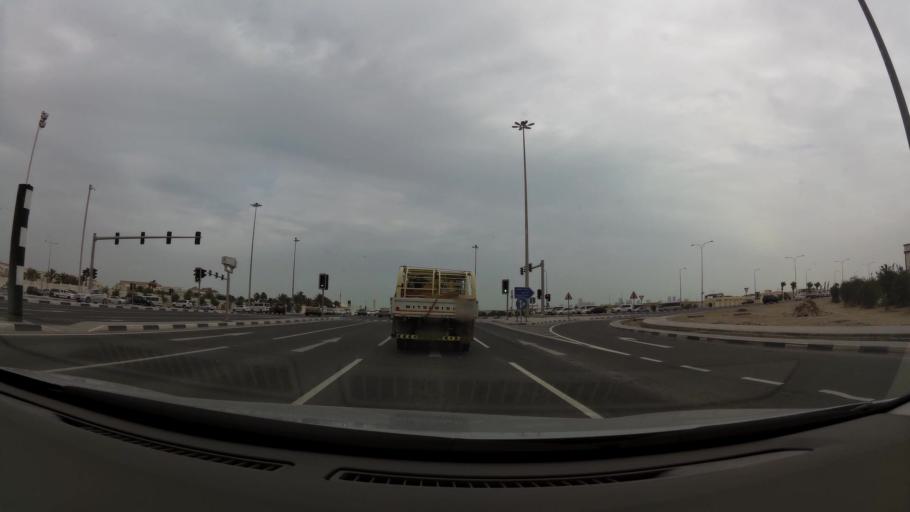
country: QA
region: Baladiyat ar Rayyan
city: Ar Rayyan
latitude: 25.3491
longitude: 51.4782
